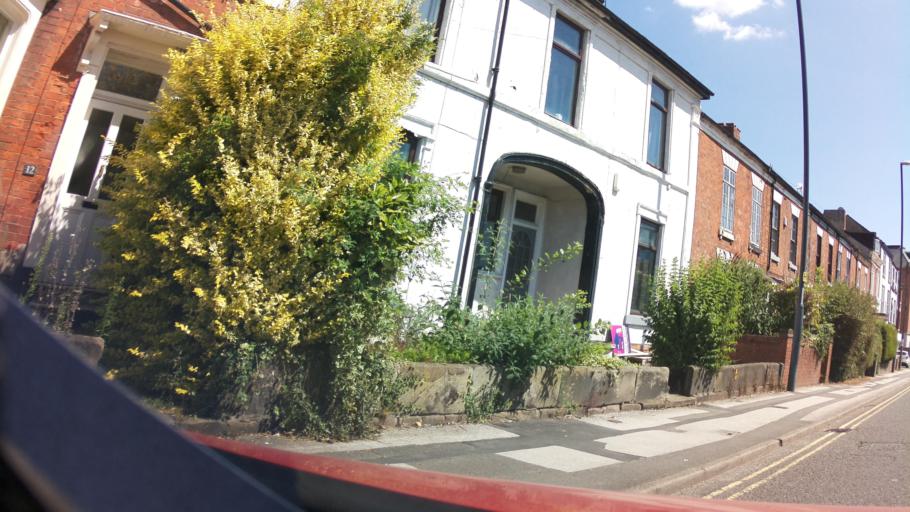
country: GB
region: England
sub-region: Derby
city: Derby
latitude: 52.9289
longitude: -1.4822
